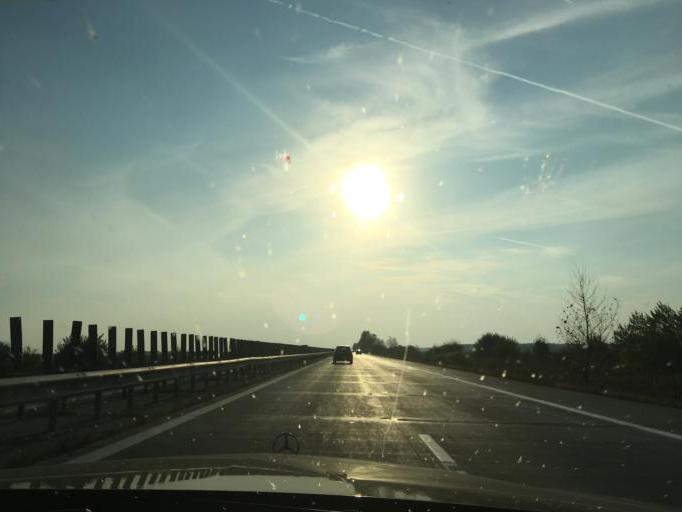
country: RO
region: Ilfov
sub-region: Comuna Branesti
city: Islaz
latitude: 44.4355
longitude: 26.3724
